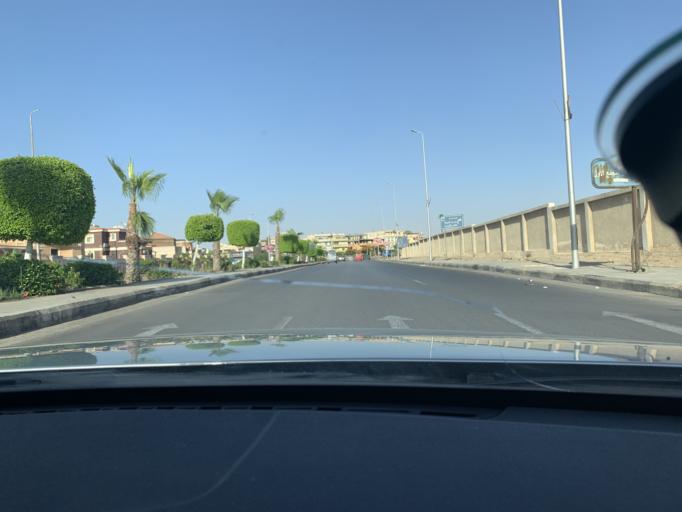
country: EG
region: Muhafazat al Qalyubiyah
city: Al Khankah
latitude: 30.0527
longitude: 31.4395
